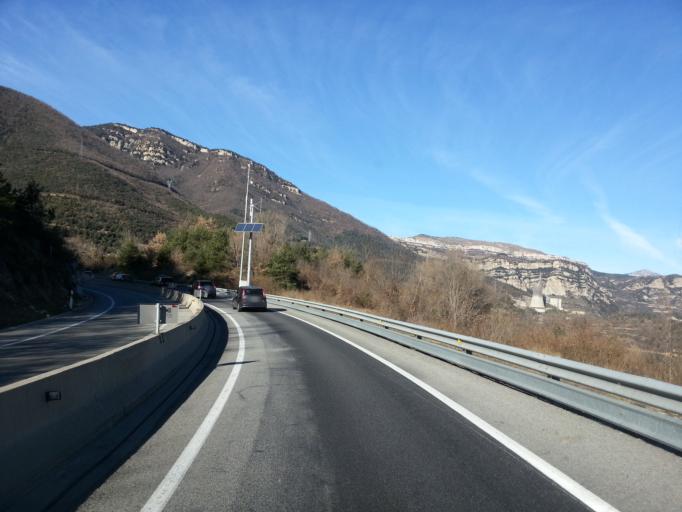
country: ES
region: Catalonia
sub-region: Provincia de Barcelona
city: Berga
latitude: 42.1518
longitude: 1.8653
